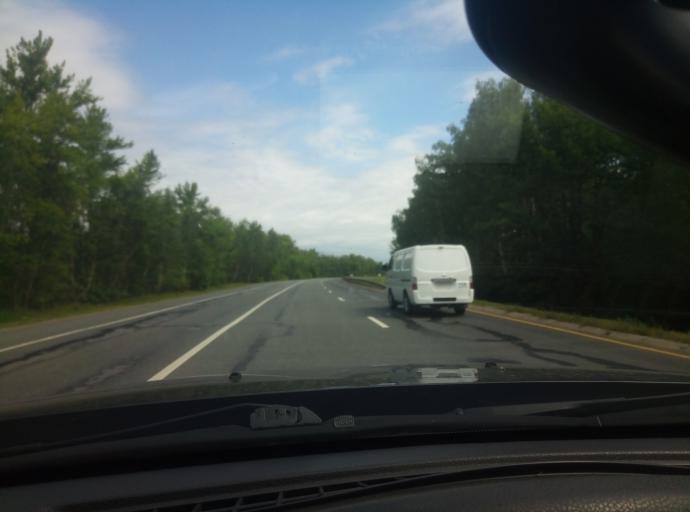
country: RU
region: Tula
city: Barsuki
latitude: 54.3045
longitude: 37.5369
